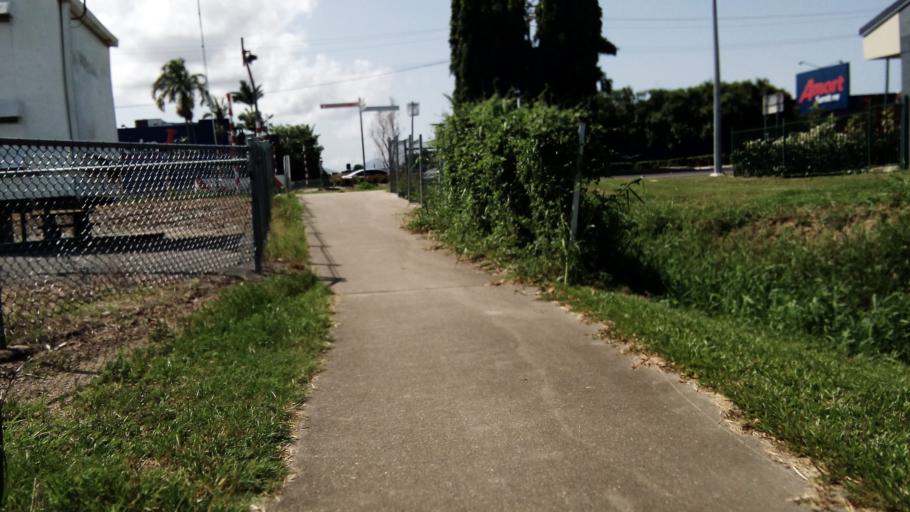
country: AU
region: Queensland
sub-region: Cairns
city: Cairns
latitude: -16.9218
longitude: 145.7683
